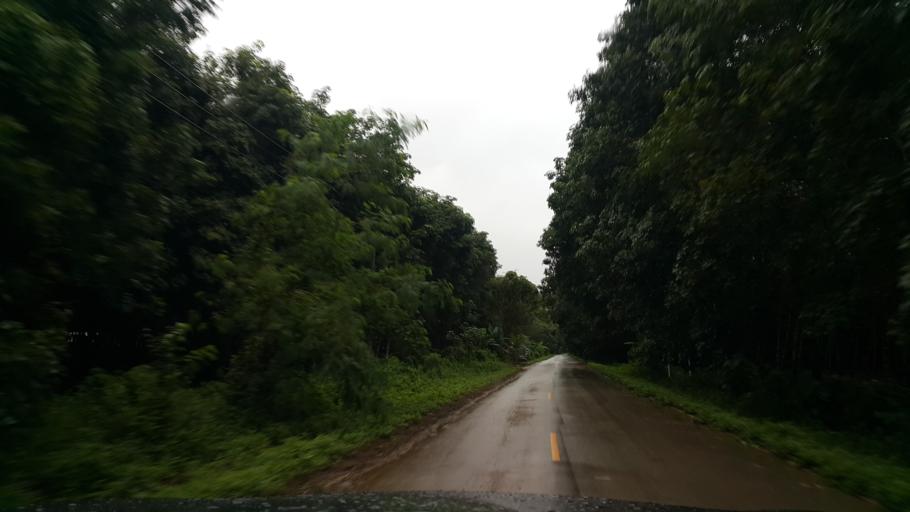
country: TH
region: Phayao
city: Phu Sang
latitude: 19.6175
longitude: 100.4055
